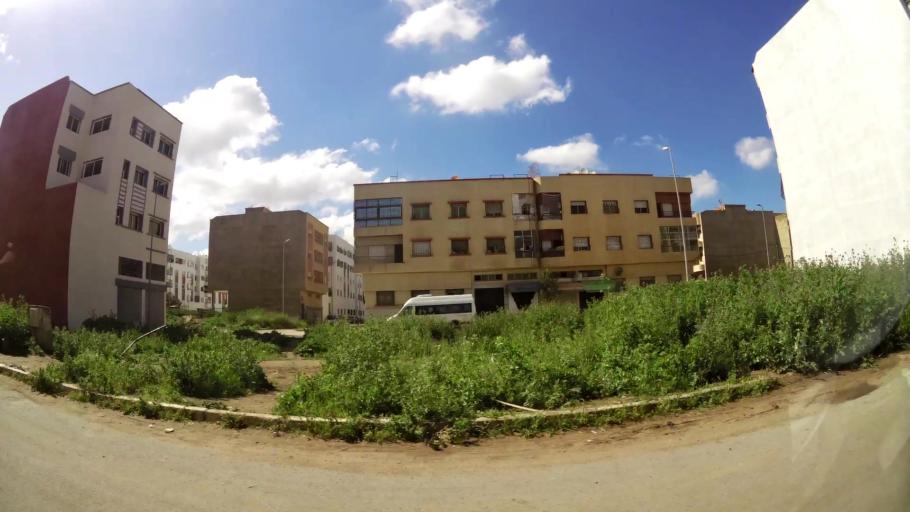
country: MA
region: Grand Casablanca
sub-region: Mediouna
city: Mediouna
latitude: 33.4573
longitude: -7.5076
